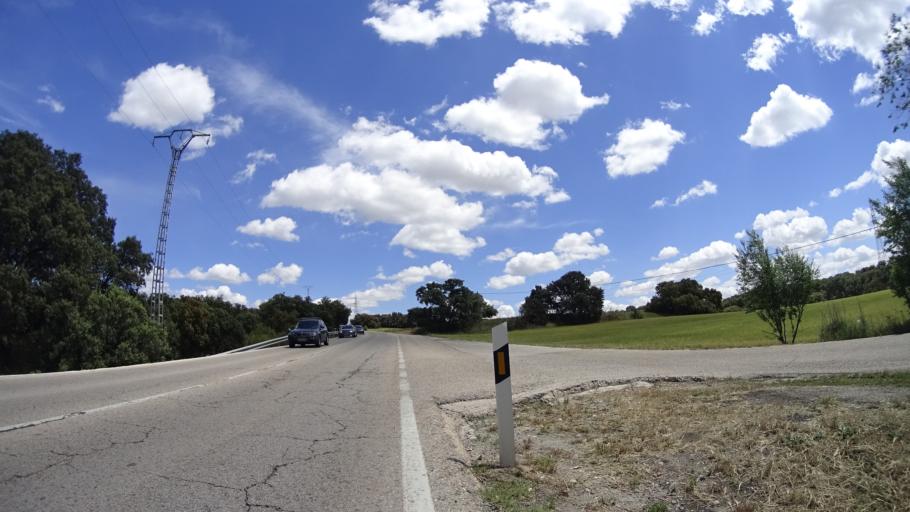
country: ES
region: Madrid
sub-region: Provincia de Madrid
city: Brunete
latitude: 40.4146
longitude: -3.9458
